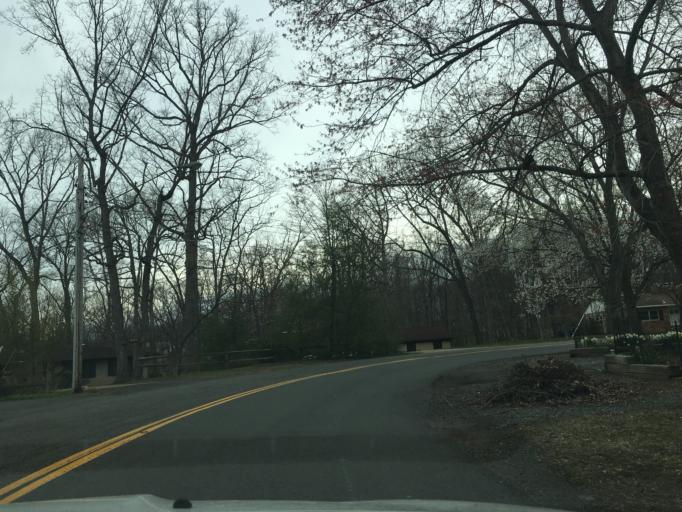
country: US
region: Virginia
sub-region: Fairfax County
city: Lake Barcroft
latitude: 38.8495
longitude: -77.1465
